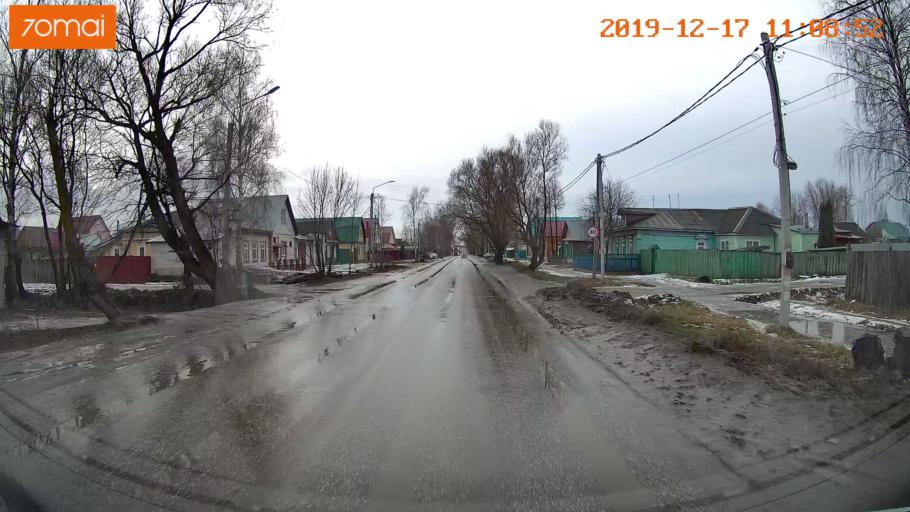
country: RU
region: Vladimir
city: Gus'-Khrustal'nyy
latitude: 55.6050
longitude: 40.6430
